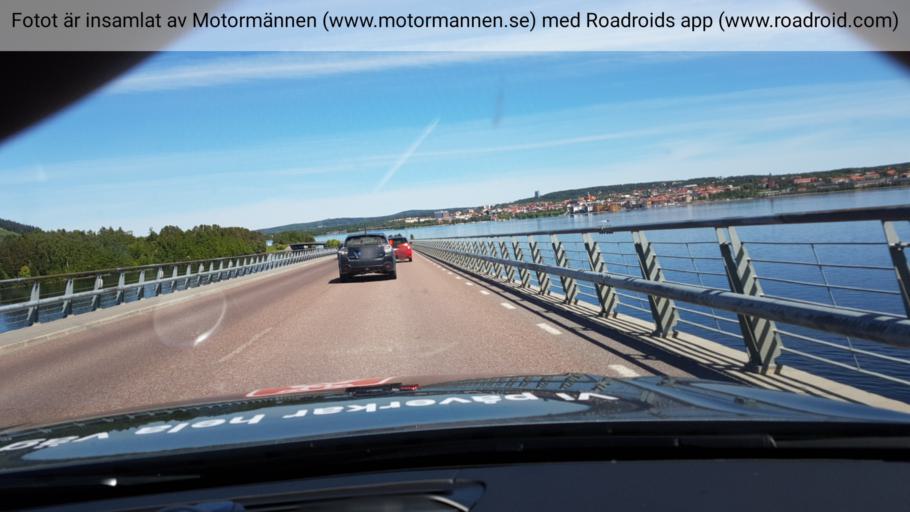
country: SE
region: Jaemtland
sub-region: OEstersunds Kommun
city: Ostersund
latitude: 63.1611
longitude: 14.6024
